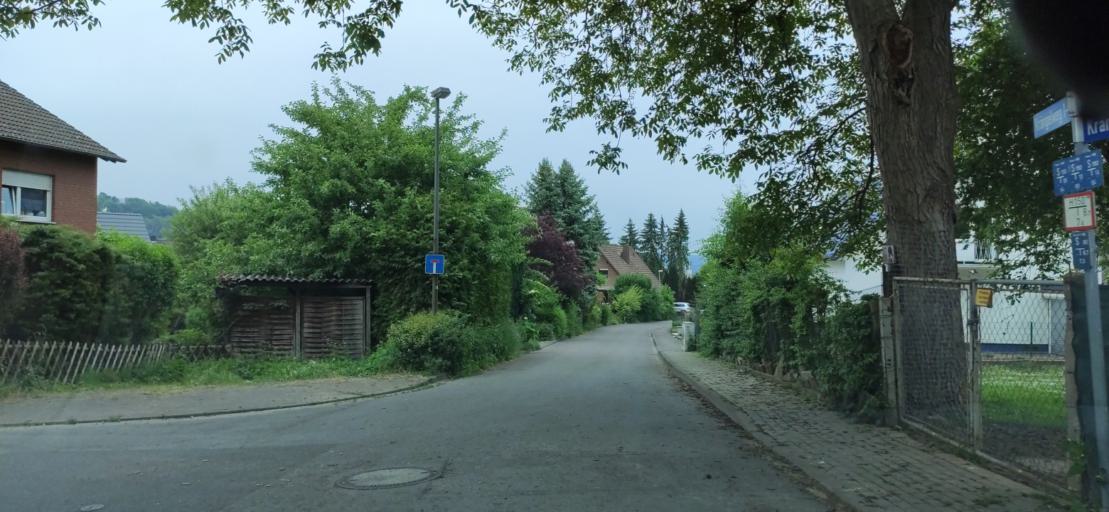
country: DE
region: North Rhine-Westphalia
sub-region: Regierungsbezirk Detmold
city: Hoexter
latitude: 51.7680
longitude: 9.3593
